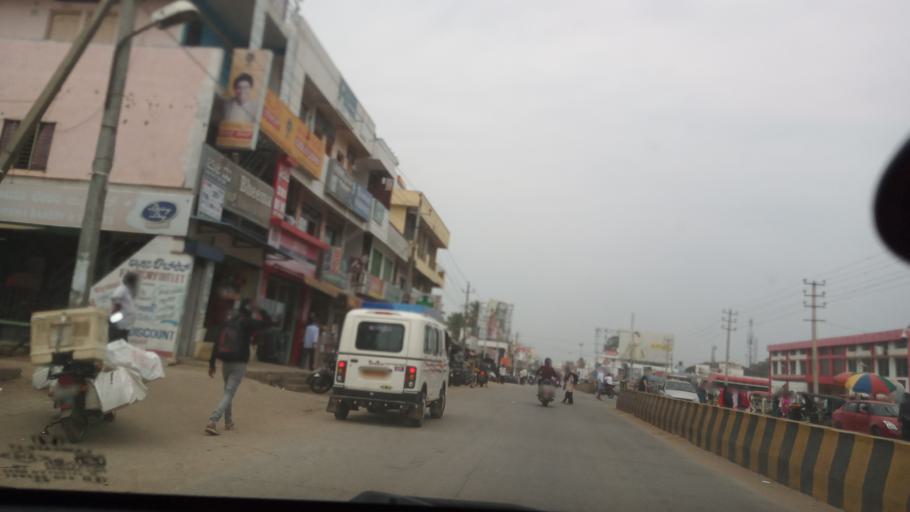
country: IN
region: Karnataka
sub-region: Chamrajnagar
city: Chamrajnagar
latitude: 11.9234
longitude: 76.9399
